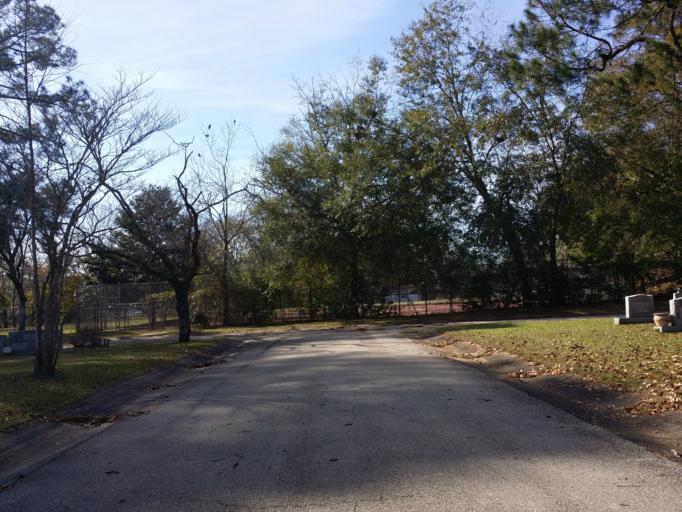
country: US
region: Florida
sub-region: Leon County
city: Tallahassee
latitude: 30.4523
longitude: -84.2869
